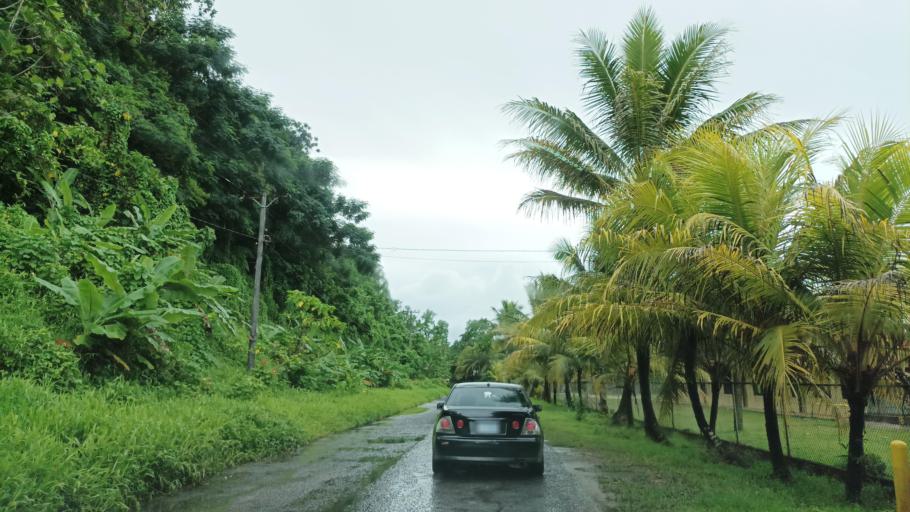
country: FM
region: Pohnpei
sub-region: Sokehs Municipality
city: Palikir - National Government Center
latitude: 6.8412
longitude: 158.1555
